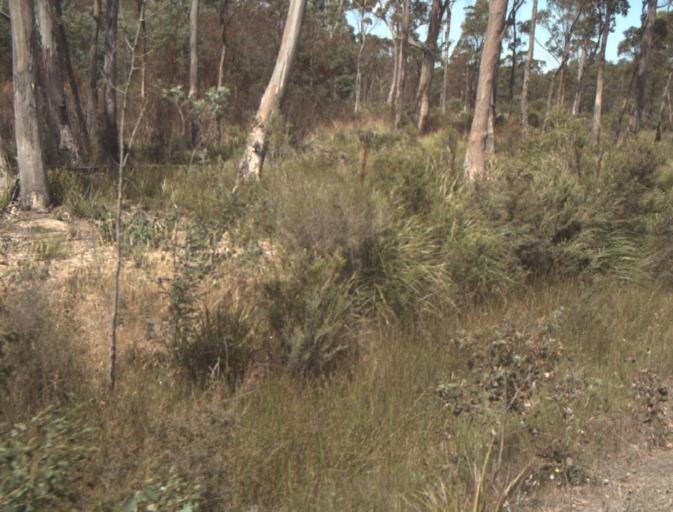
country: AU
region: Tasmania
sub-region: Launceston
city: Mayfield
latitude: -41.2752
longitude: 147.0989
